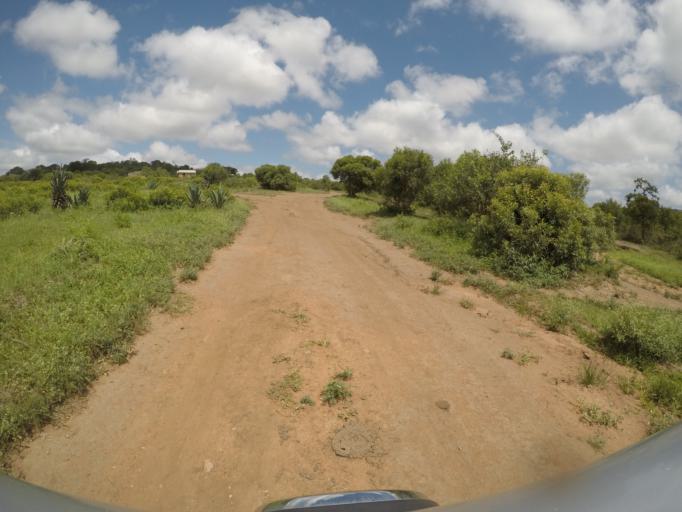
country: ZA
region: KwaZulu-Natal
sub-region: uThungulu District Municipality
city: Empangeni
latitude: -28.5812
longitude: 31.8362
